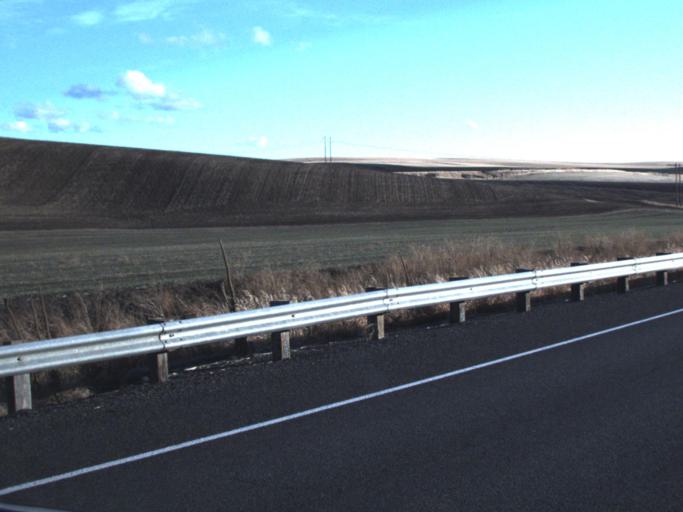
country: US
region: Washington
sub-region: Walla Walla County
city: Waitsburg
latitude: 46.2107
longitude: -118.1376
